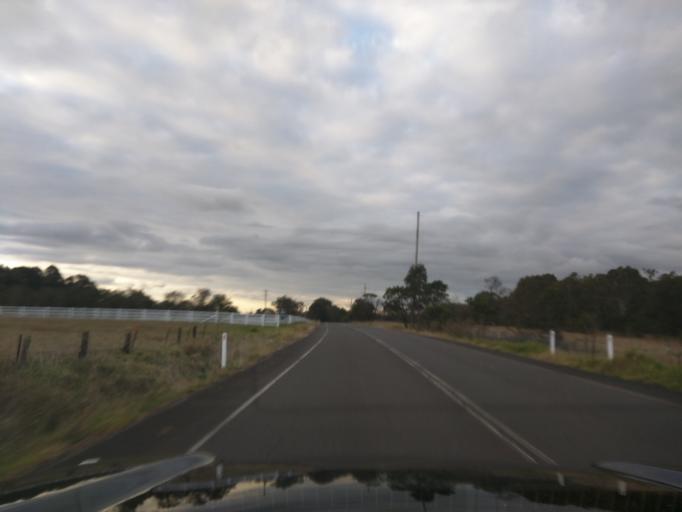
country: AU
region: New South Wales
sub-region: Wollondilly
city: Douglas Park
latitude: -34.2606
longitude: 150.7207
